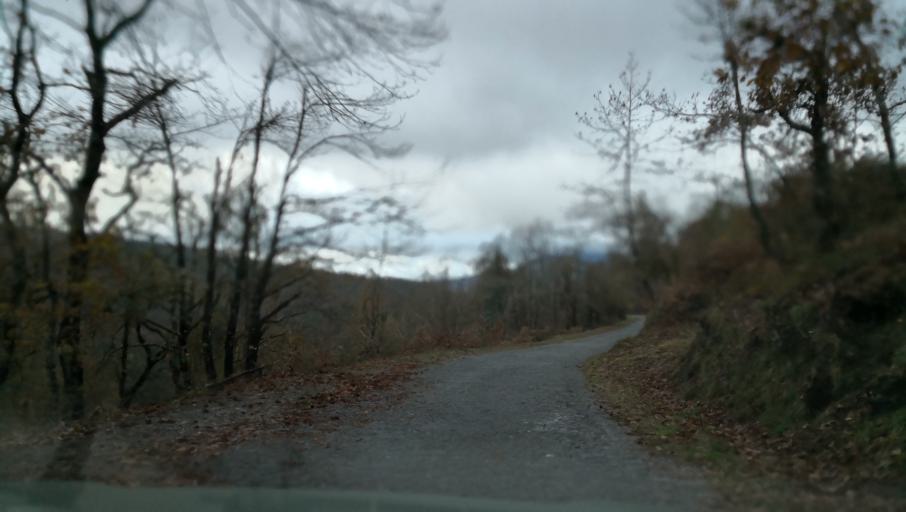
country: PT
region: Vila Real
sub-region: Santa Marta de Penaguiao
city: Santa Marta de Penaguiao
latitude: 41.3135
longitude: -7.8672
